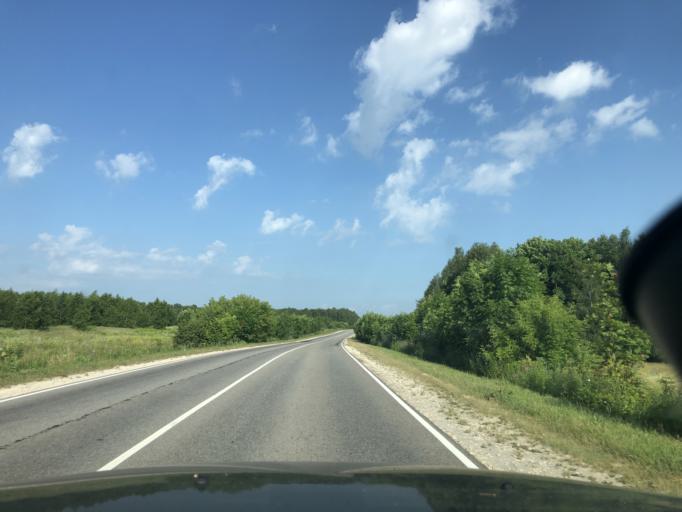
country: RU
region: Tula
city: Dubna
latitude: 54.1330
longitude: 37.0273
